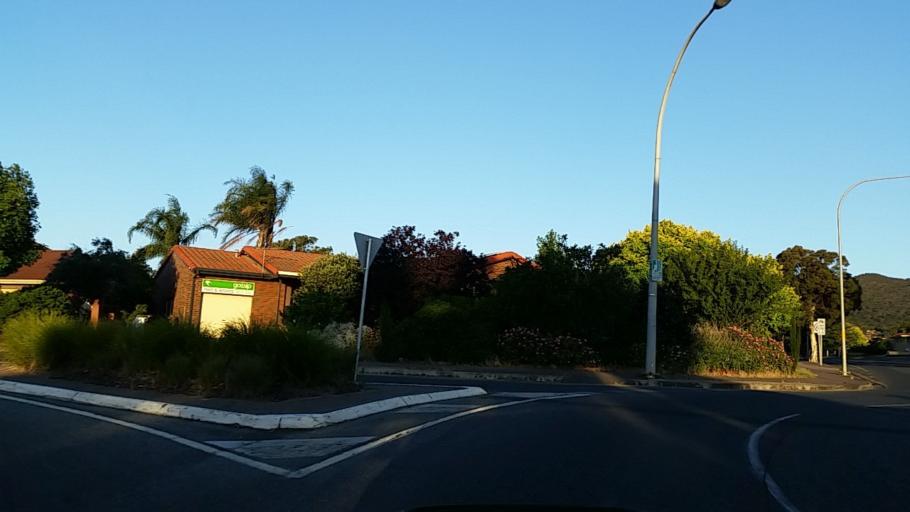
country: AU
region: South Australia
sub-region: Campbelltown
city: Athelstone
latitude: -34.8773
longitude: 138.6911
